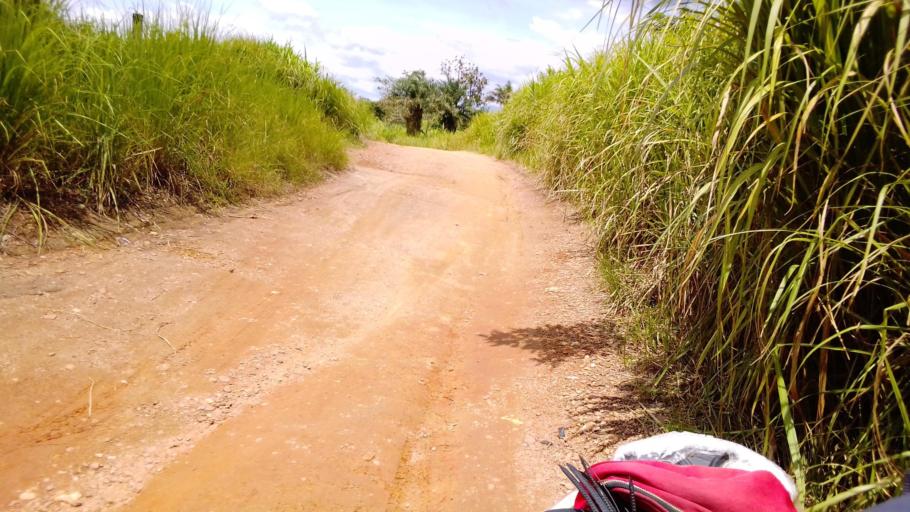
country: SL
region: Eastern Province
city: Koidu
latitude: 8.6845
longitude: -10.9565
